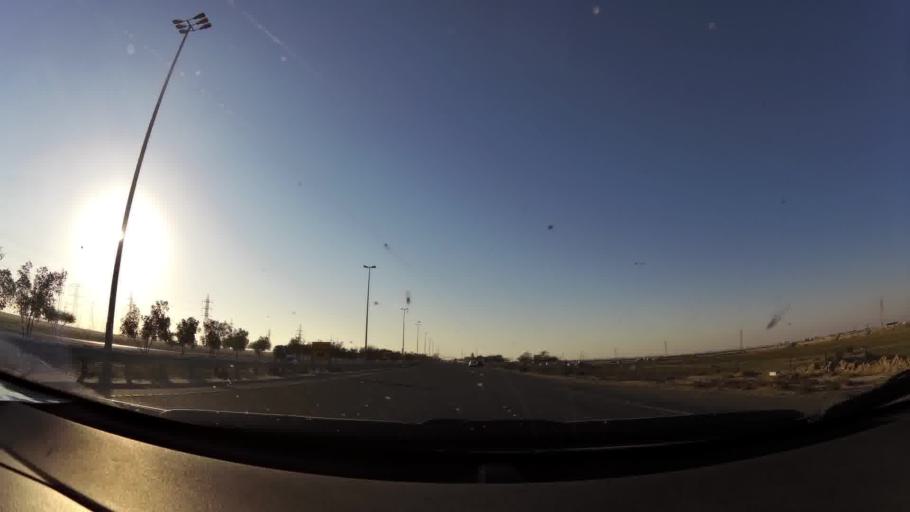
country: KW
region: Al Ahmadi
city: Al Fahahil
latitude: 28.7514
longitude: 48.2816
